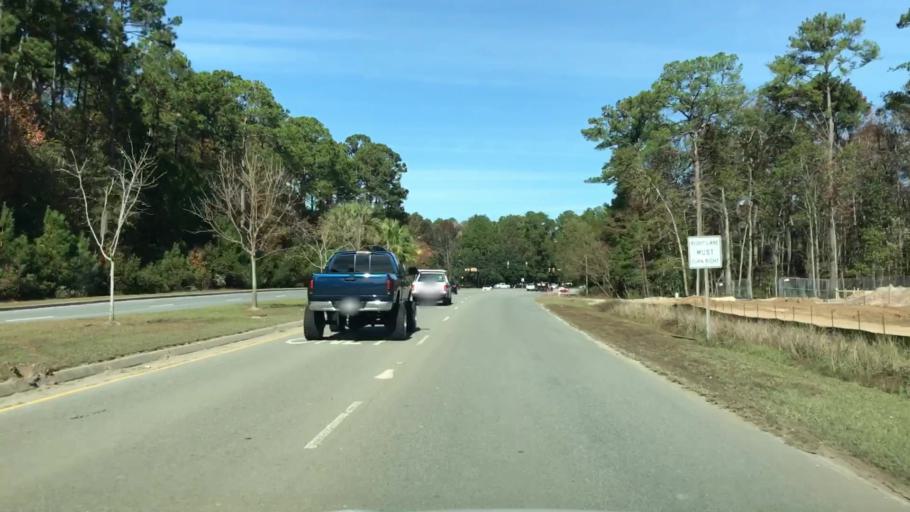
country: US
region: South Carolina
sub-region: Beaufort County
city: Bluffton
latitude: 32.2886
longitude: -80.9090
